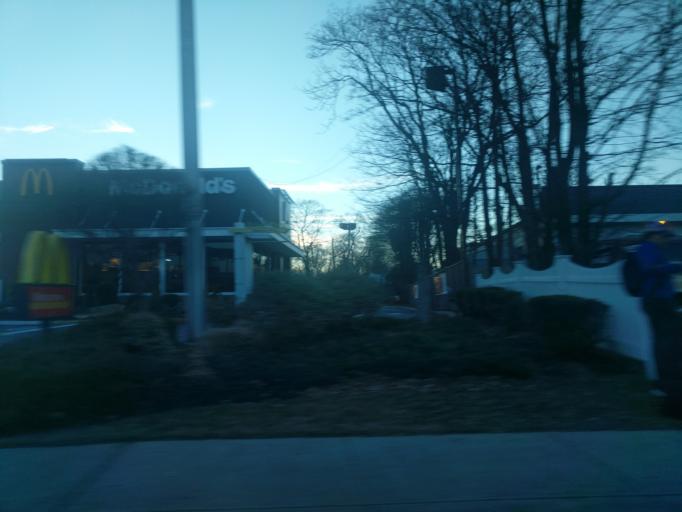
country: US
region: New York
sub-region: Nassau County
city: Wantagh
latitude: 40.6733
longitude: -73.5102
